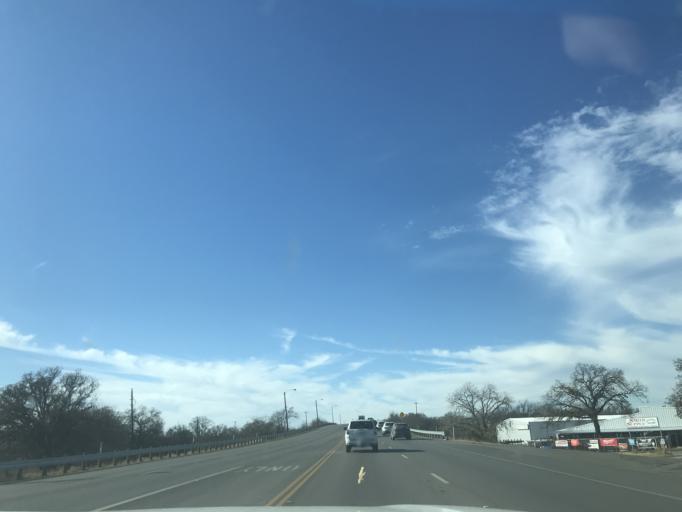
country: US
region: Texas
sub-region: Erath County
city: Stephenville
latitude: 32.2048
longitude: -98.2155
